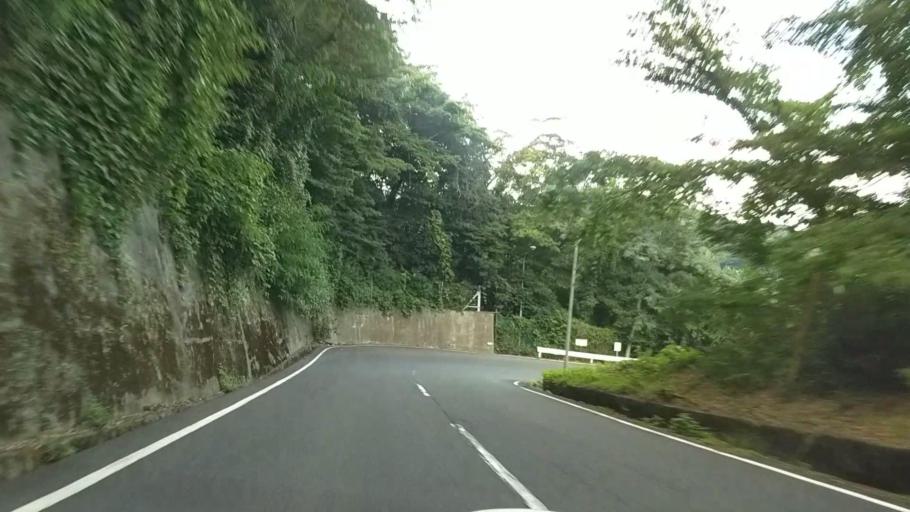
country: JP
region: Yamanashi
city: Uenohara
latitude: 35.6167
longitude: 139.1327
